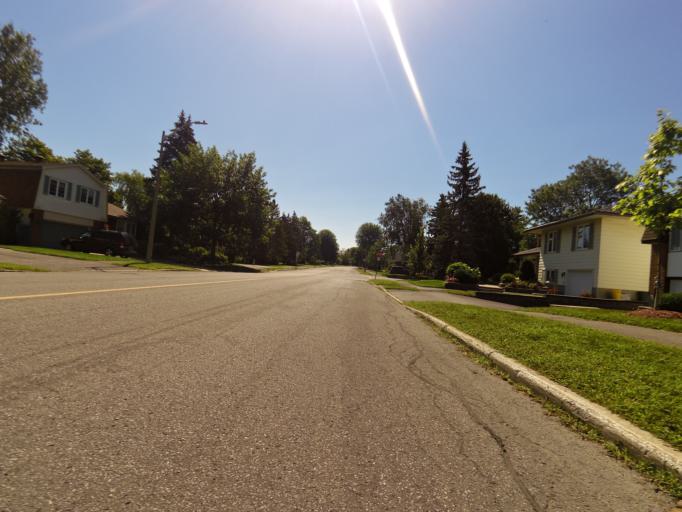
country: CA
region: Ontario
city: Ottawa
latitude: 45.3543
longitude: -75.6601
